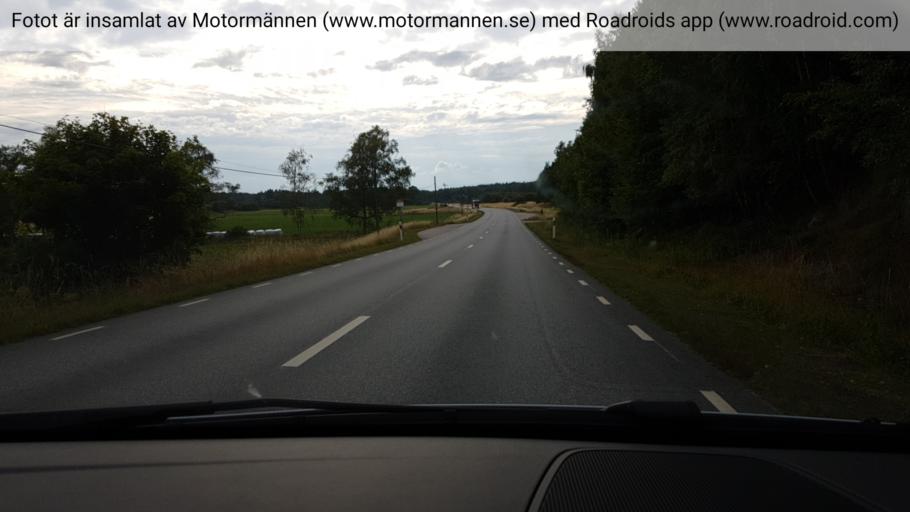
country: SE
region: Stockholm
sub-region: Norrtalje Kommun
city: Skanninge
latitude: 59.8951
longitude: 18.4466
